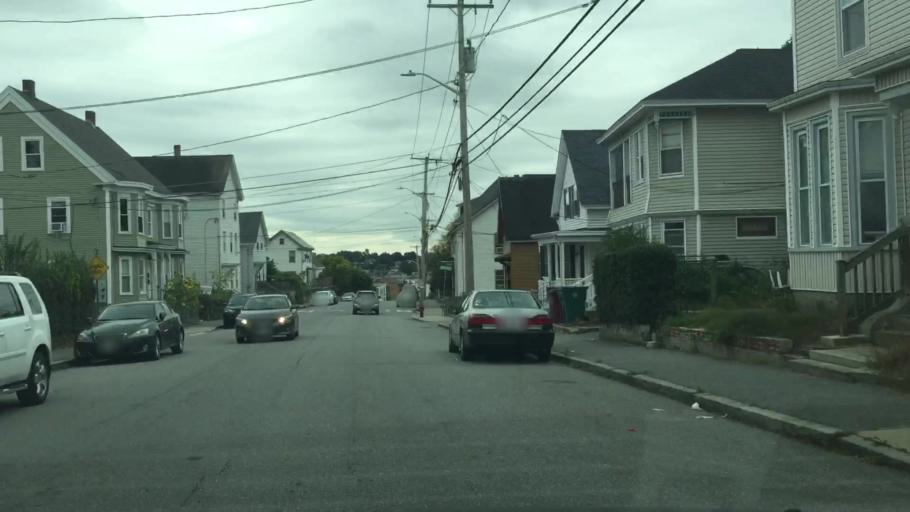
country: US
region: Massachusetts
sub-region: Middlesex County
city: Lowell
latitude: 42.6458
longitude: -71.3268
